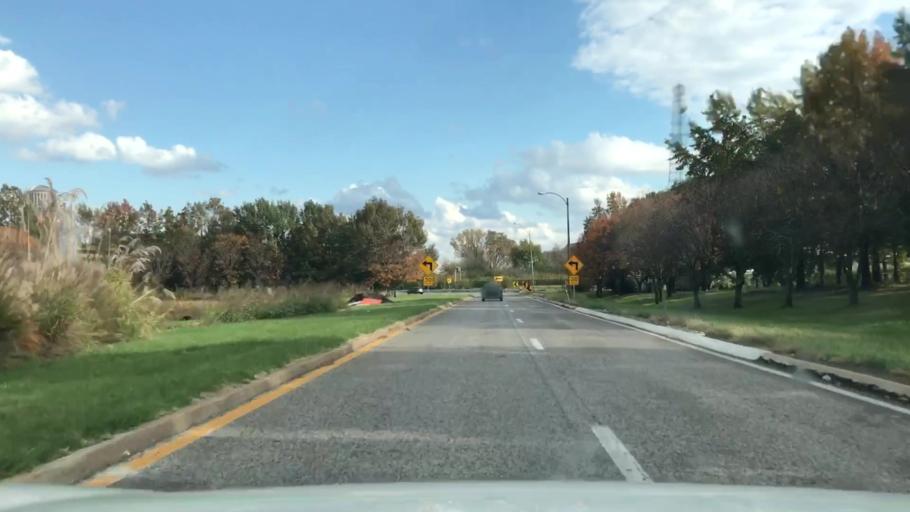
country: US
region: Missouri
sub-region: City of Saint Louis
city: St. Louis
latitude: 38.6262
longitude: -90.2148
